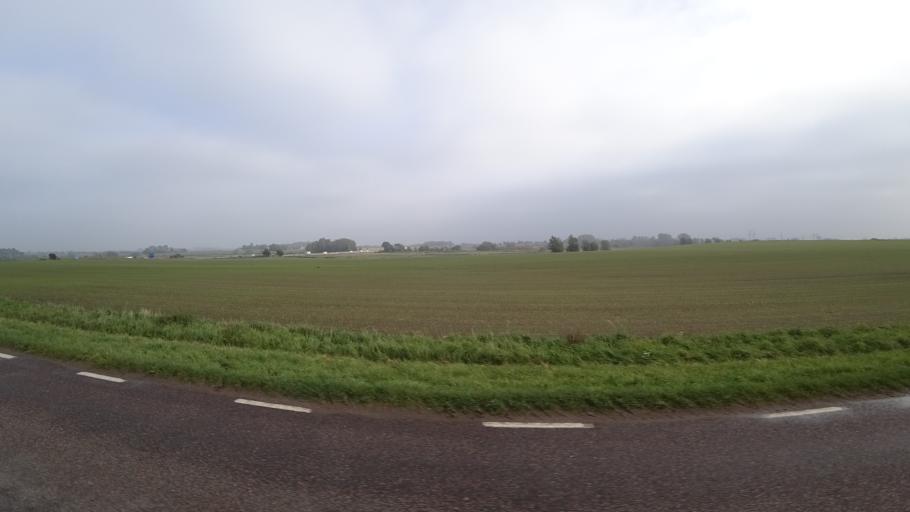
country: SE
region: Skane
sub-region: Kavlinge Kommun
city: Loddekopinge
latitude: 55.7502
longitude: 13.0059
